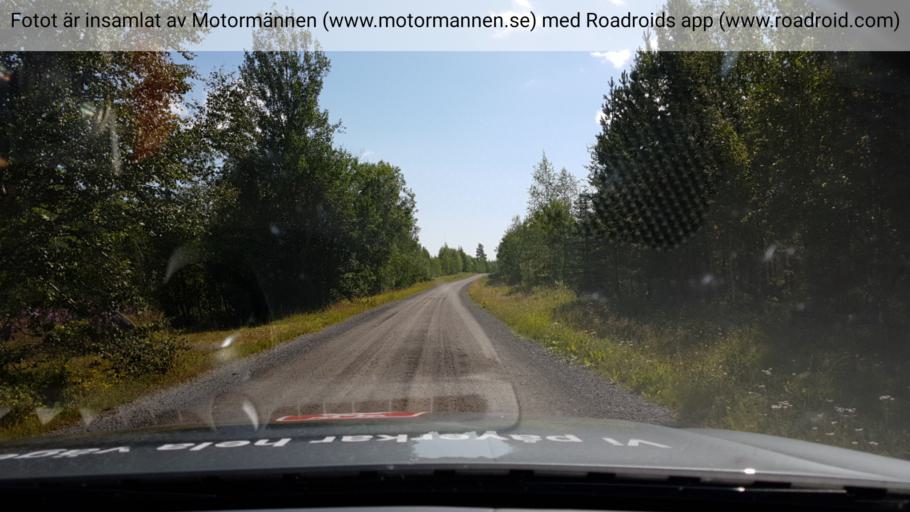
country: SE
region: Jaemtland
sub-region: Stroemsunds Kommun
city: Stroemsund
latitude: 63.3492
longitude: 15.3644
